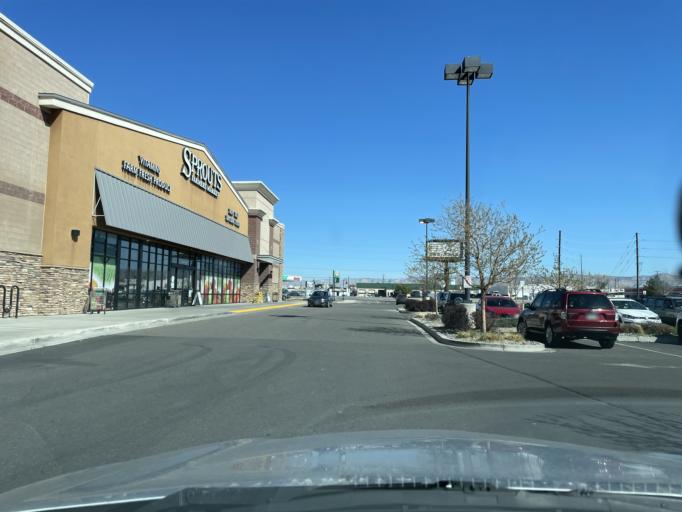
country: US
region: Colorado
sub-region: Mesa County
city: Grand Junction
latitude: 39.0802
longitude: -108.5861
